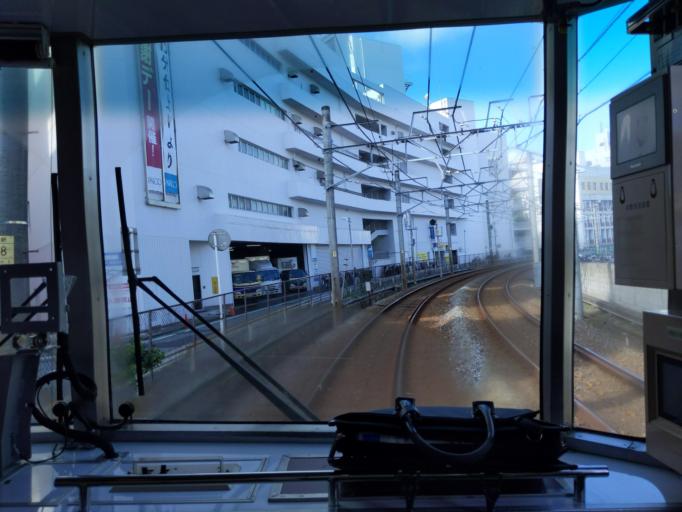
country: JP
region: Chiba
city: Funabashi
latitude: 35.6915
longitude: 140.0222
